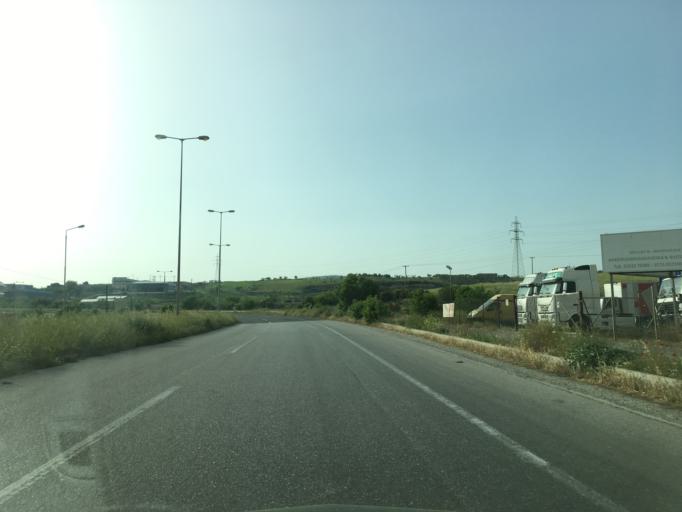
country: GR
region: Thessaly
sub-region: Nomos Magnisias
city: Nea Ionia
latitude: 39.3818
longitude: 22.8627
